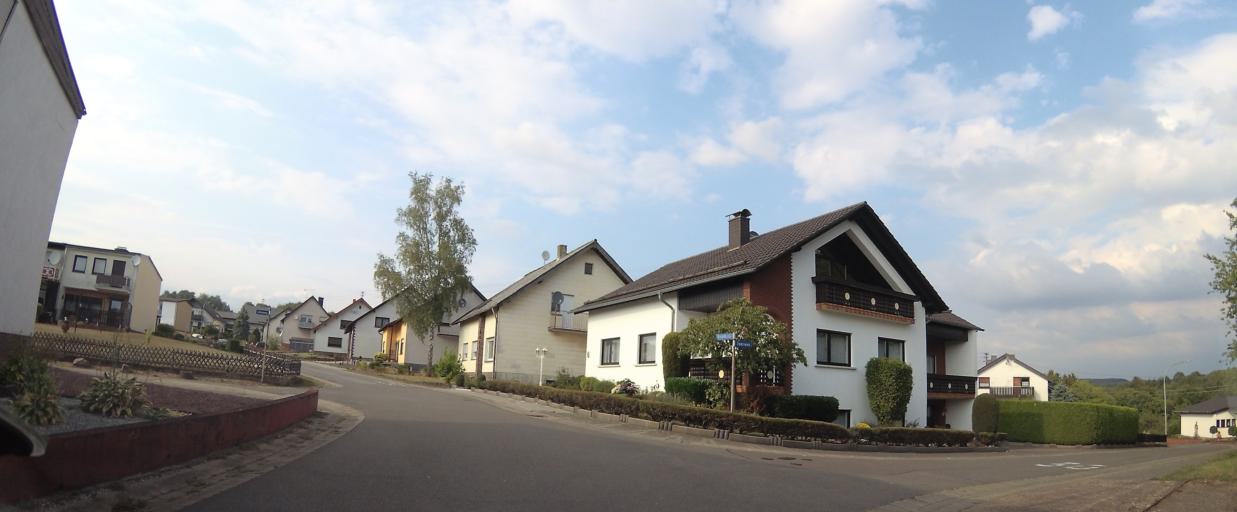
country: DE
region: Saarland
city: Wadern
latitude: 49.5290
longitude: 6.9293
